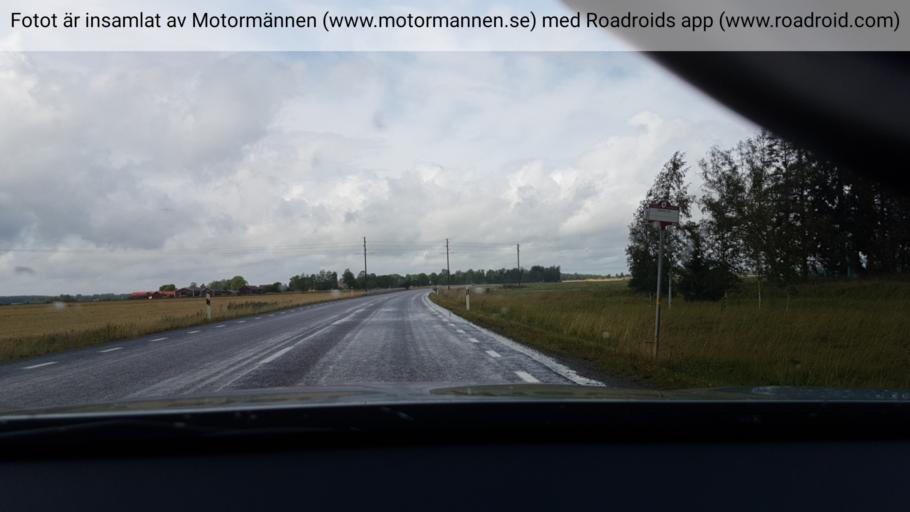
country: SE
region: Uppsala
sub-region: Osthammars Kommun
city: Bjorklinge
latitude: 59.9182
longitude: 17.5092
